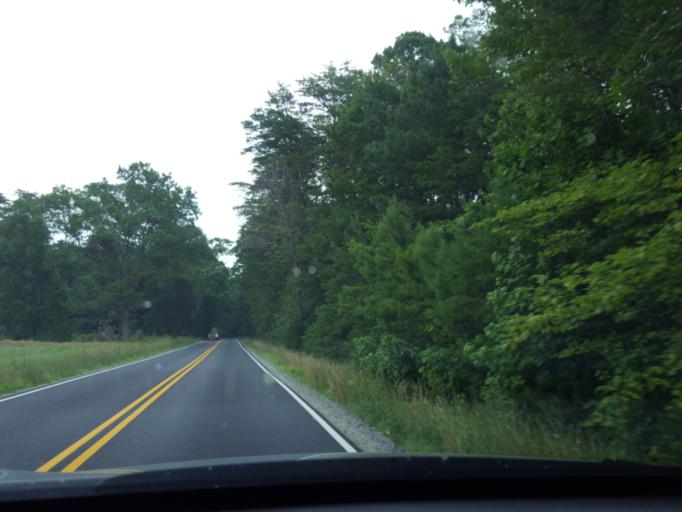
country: US
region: Virginia
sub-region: Spotsylvania County
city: Spotsylvania
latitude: 38.2905
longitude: -77.7238
